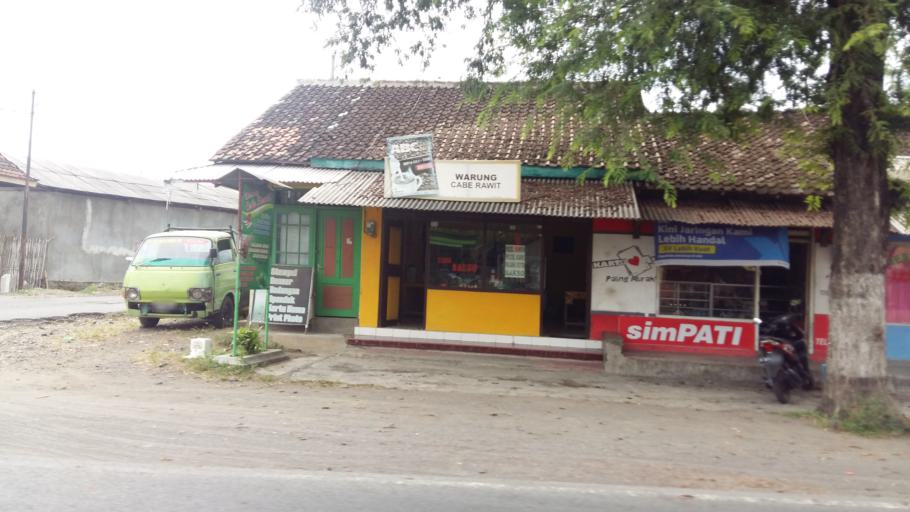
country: ID
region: East Java
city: Krajan
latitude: -8.3266
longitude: 114.2823
